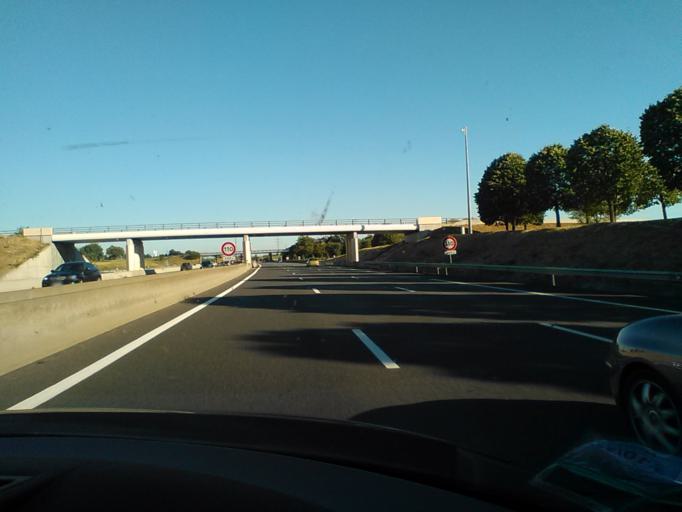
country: FR
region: Rhone-Alpes
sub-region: Departement du Rhone
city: Montanay
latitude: 45.8849
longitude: 4.8950
